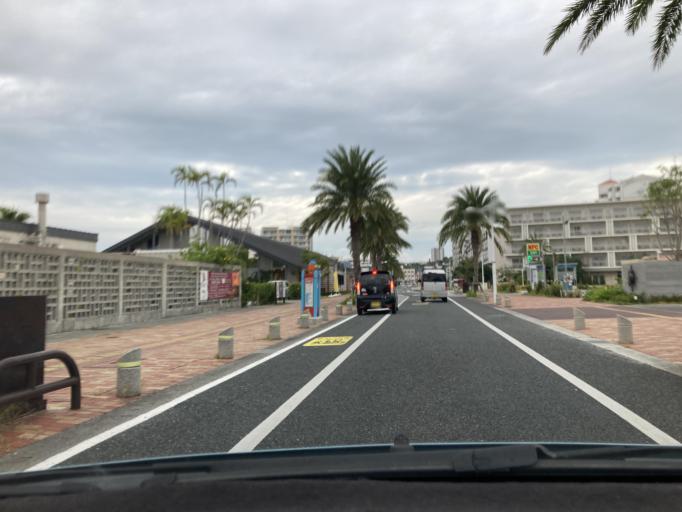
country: JP
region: Okinawa
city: Chatan
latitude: 26.3208
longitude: 127.7540
